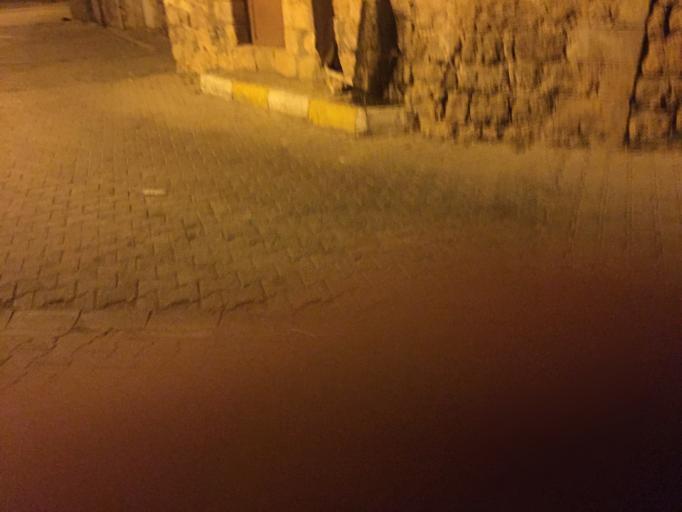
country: TR
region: Mardin
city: Kindirip
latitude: 37.4466
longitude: 41.2190
